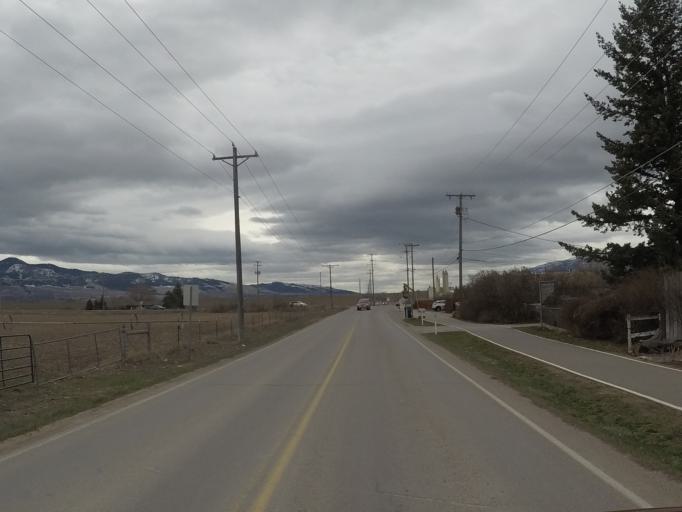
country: US
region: Montana
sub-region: Missoula County
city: Orchard Homes
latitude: 46.8889
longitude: -114.0553
